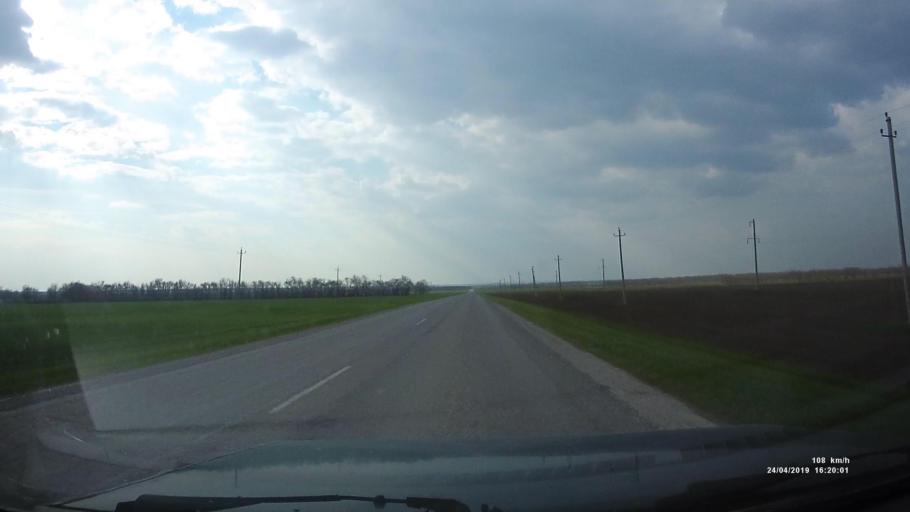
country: RU
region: Rostov
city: Orlovskiy
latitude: 46.7881
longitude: 42.0865
